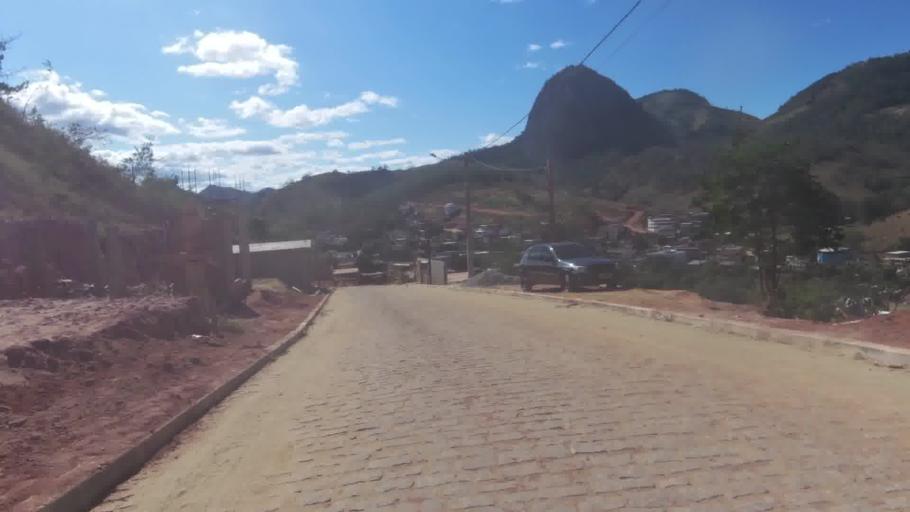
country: BR
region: Espirito Santo
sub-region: Cachoeiro De Itapemirim
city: Cachoeiro de Itapemirim
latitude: -20.9195
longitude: -41.1918
